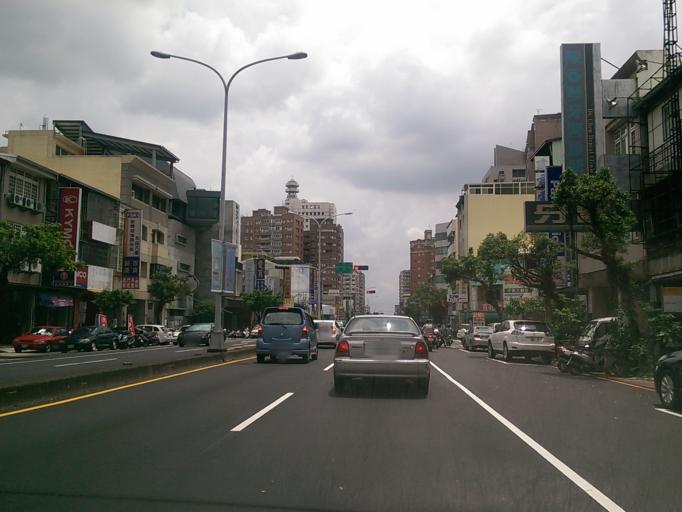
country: TW
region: Taiwan
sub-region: Taichung City
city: Taichung
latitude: 24.1574
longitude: 120.6943
